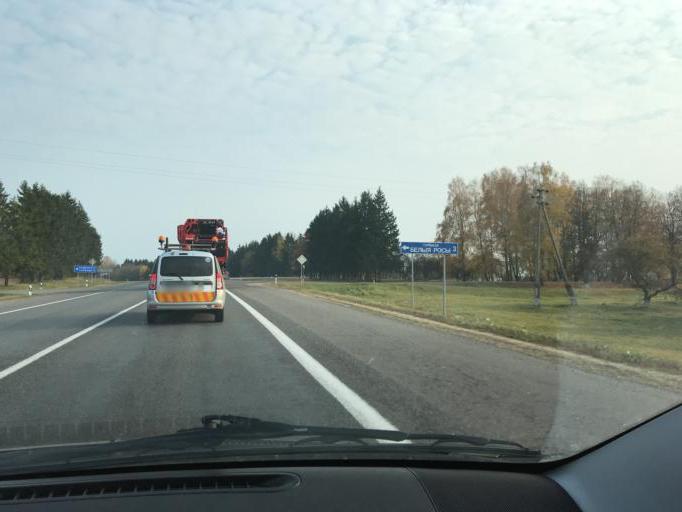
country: BY
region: Vitebsk
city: Haradok
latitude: 55.1438
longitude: 29.8458
